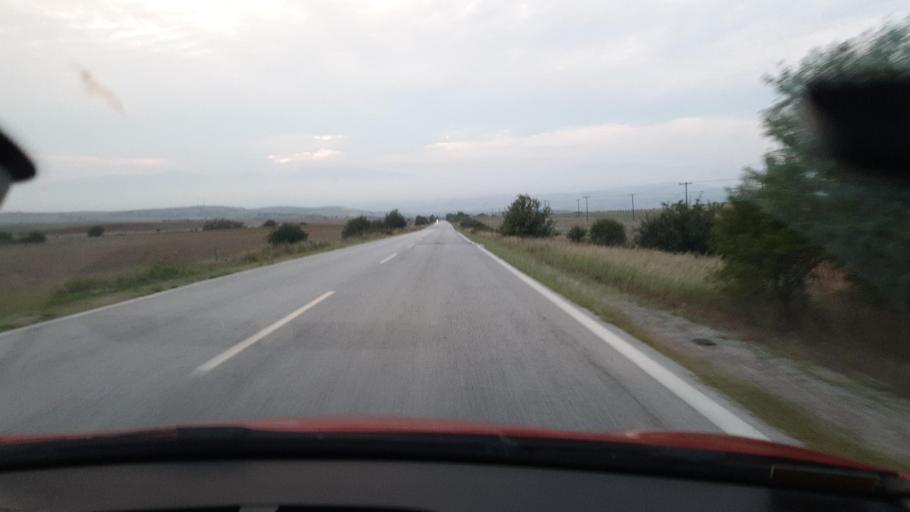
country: GR
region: Central Macedonia
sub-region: Nomos Kilkis
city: Polykastro
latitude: 41.0066
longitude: 22.7000
